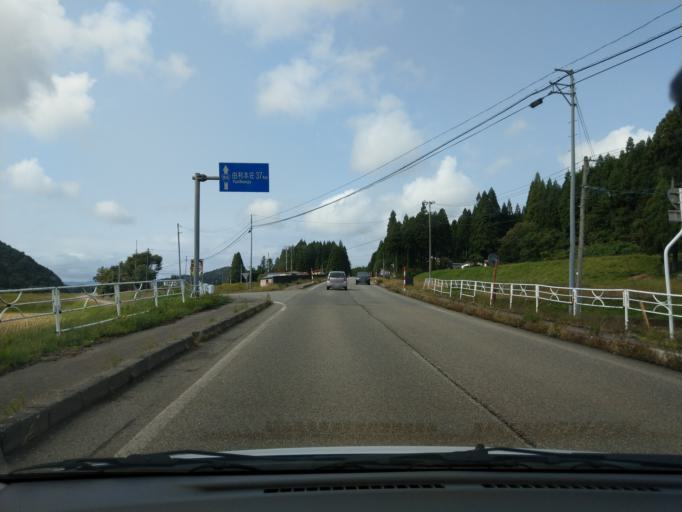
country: JP
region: Akita
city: Omagari
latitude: 39.4413
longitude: 140.3487
